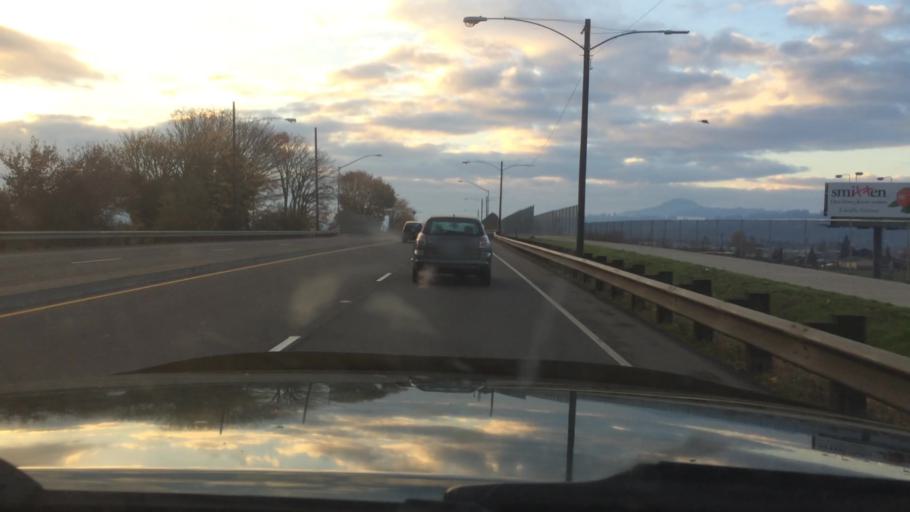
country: US
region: Oregon
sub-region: Lane County
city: Eugene
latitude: 44.0614
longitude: -123.1348
